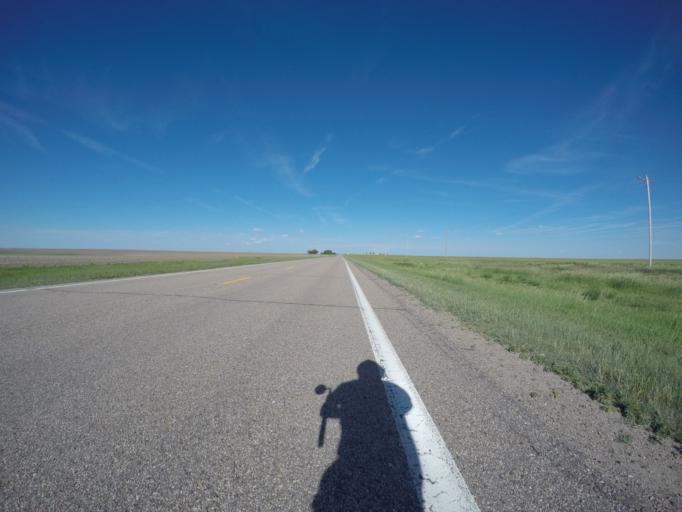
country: US
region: Kansas
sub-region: Cheyenne County
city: Saint Francis
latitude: 39.7565
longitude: -102.0020
